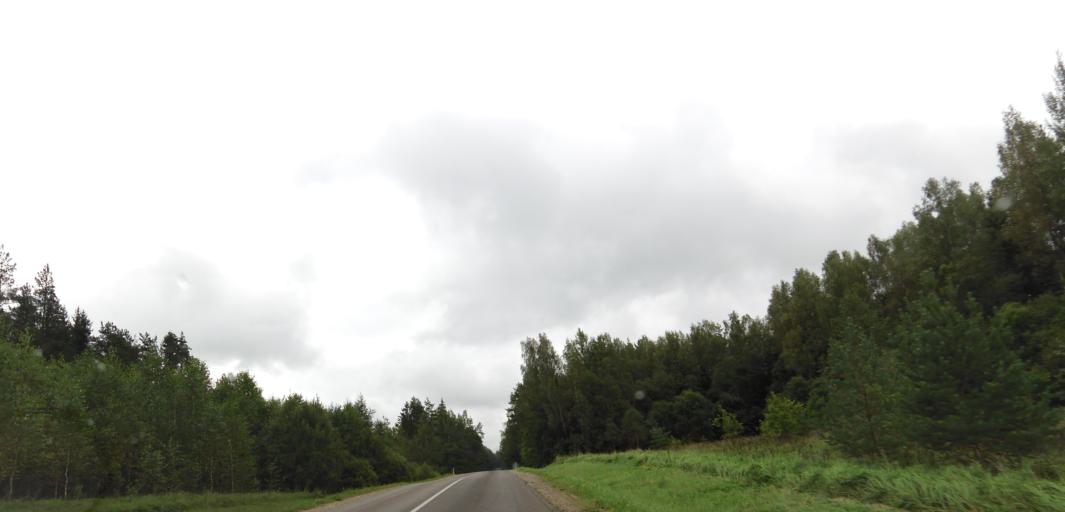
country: LT
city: Moletai
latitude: 55.3155
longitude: 25.3324
